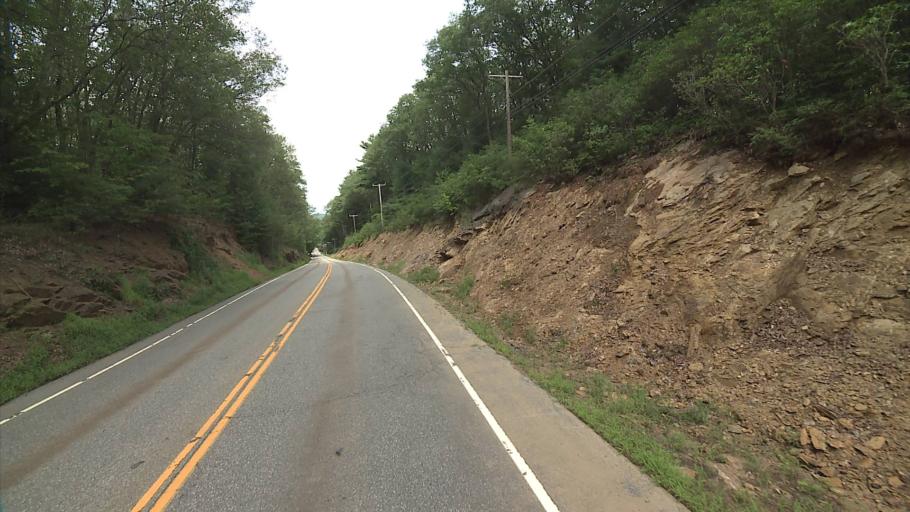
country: US
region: Massachusetts
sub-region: Hampden County
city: Holland
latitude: 42.0019
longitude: -72.1496
